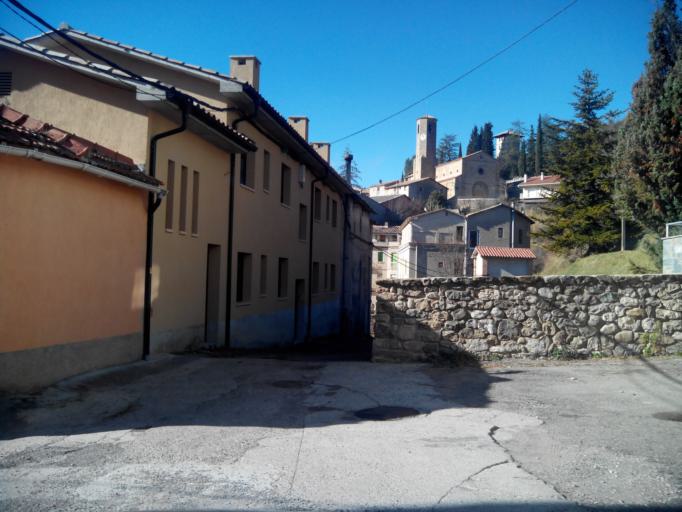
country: ES
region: Catalonia
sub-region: Provincia de Barcelona
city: Vilada
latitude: 42.1373
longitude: 1.9311
